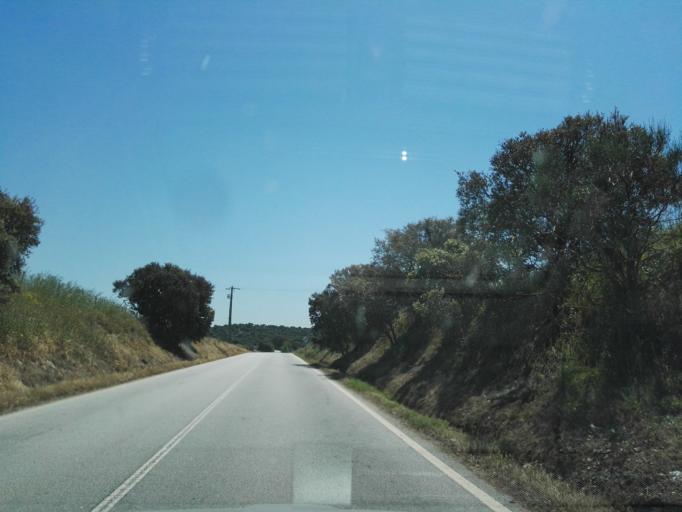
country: PT
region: Portalegre
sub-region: Arronches
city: Arronches
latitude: 39.0048
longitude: -7.2289
